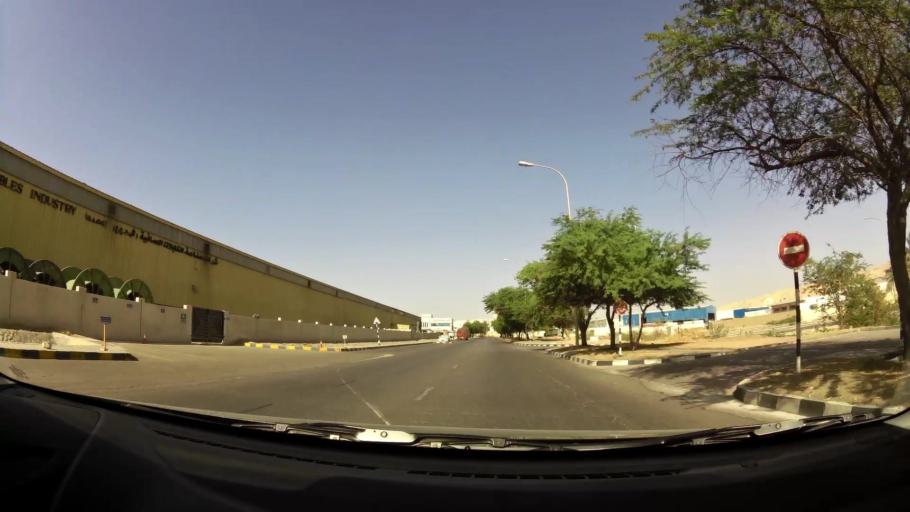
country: OM
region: Muhafazat Masqat
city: As Sib al Jadidah
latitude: 23.5576
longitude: 58.2098
